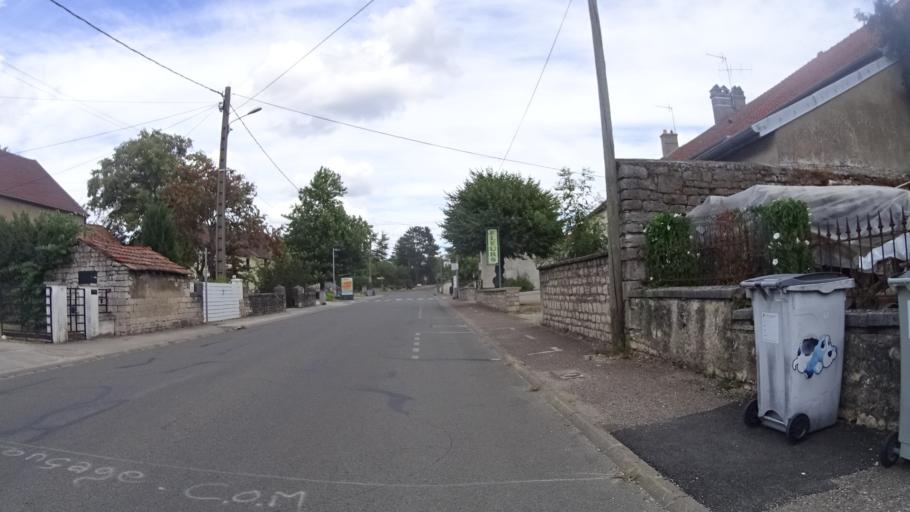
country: FR
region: Franche-Comte
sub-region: Departement du Jura
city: Damparis
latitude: 47.0728
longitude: 5.4128
